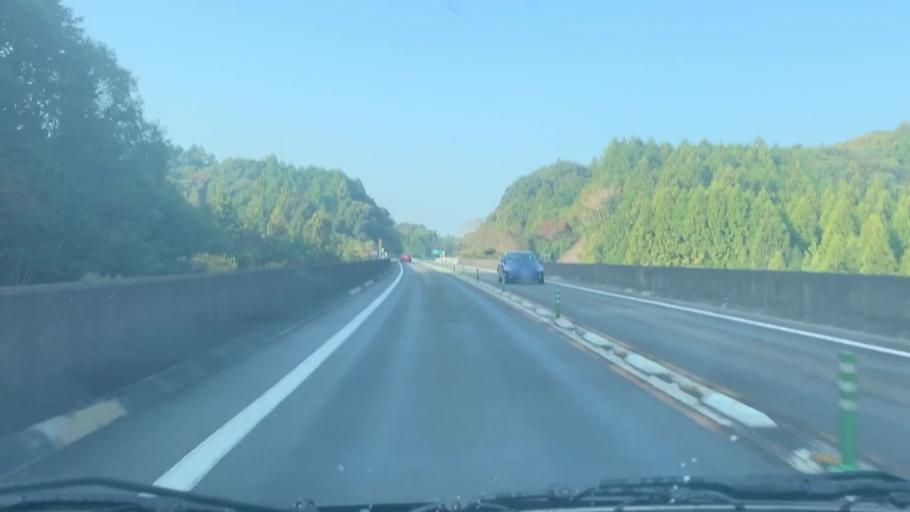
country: JP
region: Saga Prefecture
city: Ureshinomachi-shimojuku
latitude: 33.1443
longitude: 129.9644
